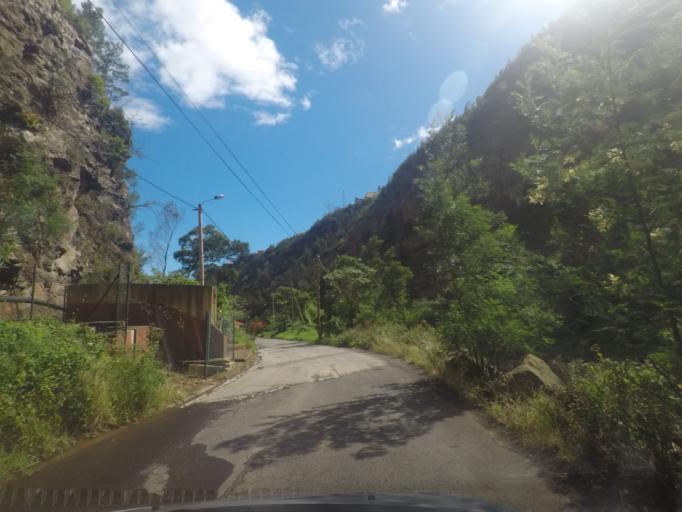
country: PT
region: Madeira
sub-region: Funchal
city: Nossa Senhora do Monte
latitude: 32.6790
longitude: -16.9175
